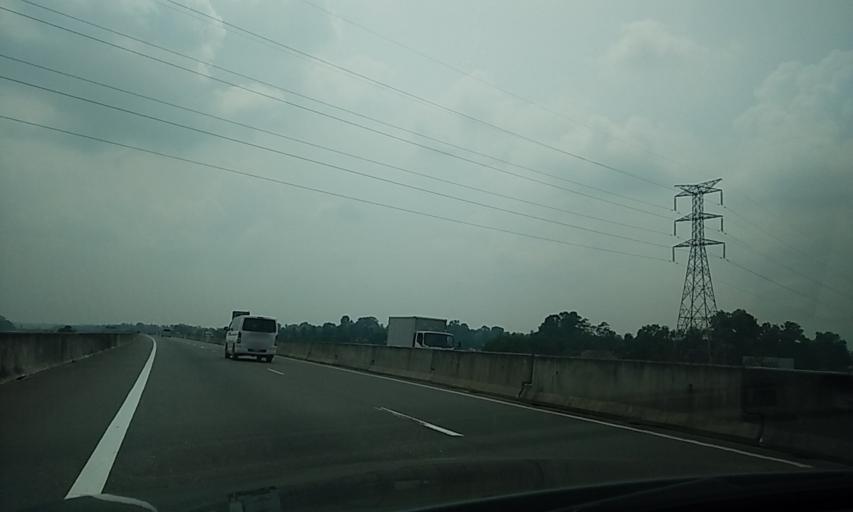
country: LK
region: Western
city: Mulleriyawa
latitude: 6.9117
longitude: 79.9821
